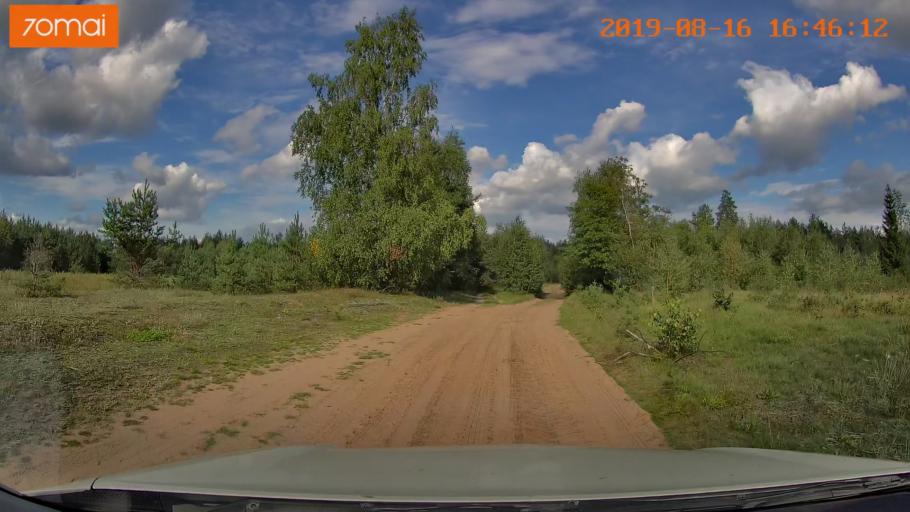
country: BY
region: Mogilev
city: Asipovichy
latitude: 53.2491
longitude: 28.7861
